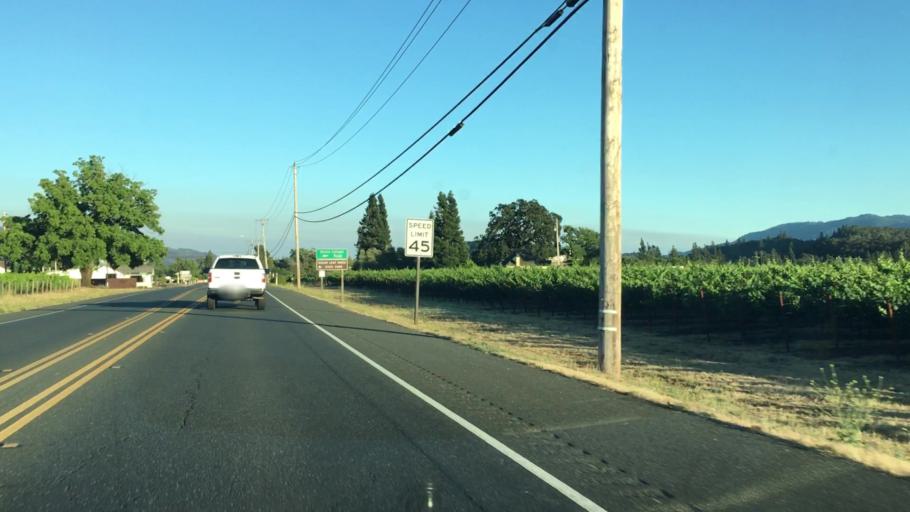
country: US
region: California
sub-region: Sonoma County
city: Kenwood
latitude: 38.4255
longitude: -122.5574
